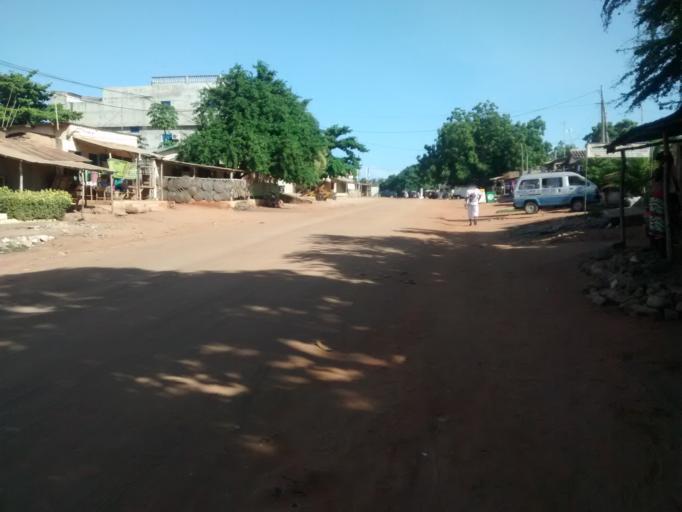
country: TG
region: Maritime
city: Lome
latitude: 6.1746
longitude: 1.1864
